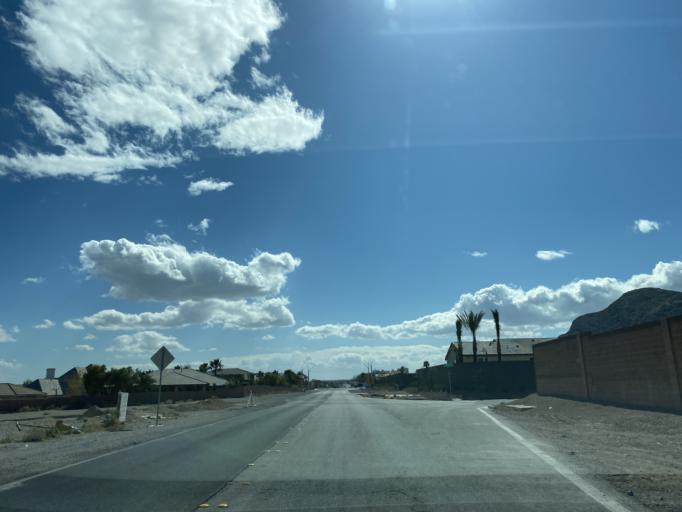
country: US
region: Nevada
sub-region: Clark County
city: Summerlin South
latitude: 36.2504
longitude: -115.3063
